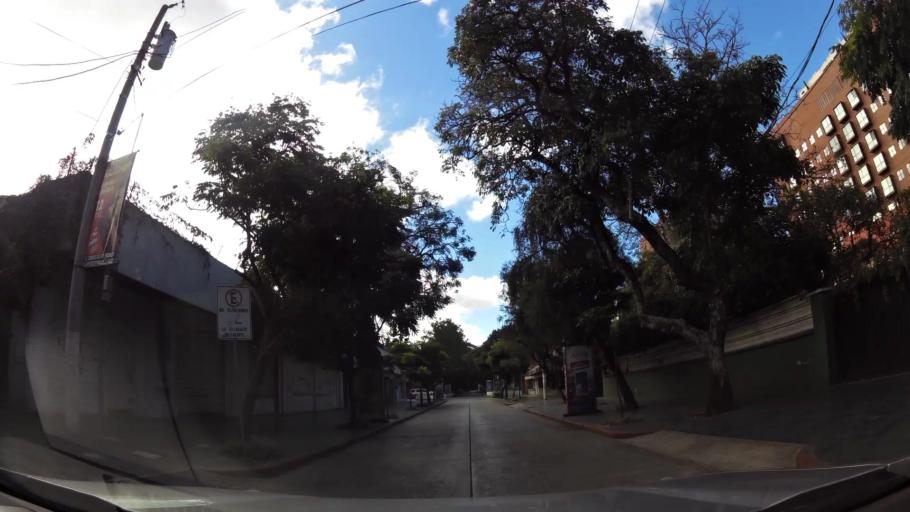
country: GT
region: Guatemala
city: Santa Catarina Pinula
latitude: 14.5974
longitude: -90.5149
